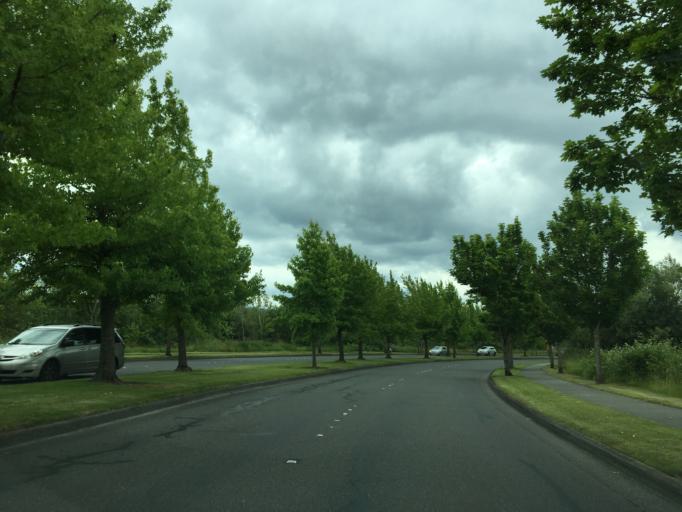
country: US
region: Washington
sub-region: Whatcom County
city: Bellingham
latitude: 48.7971
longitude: -122.4935
